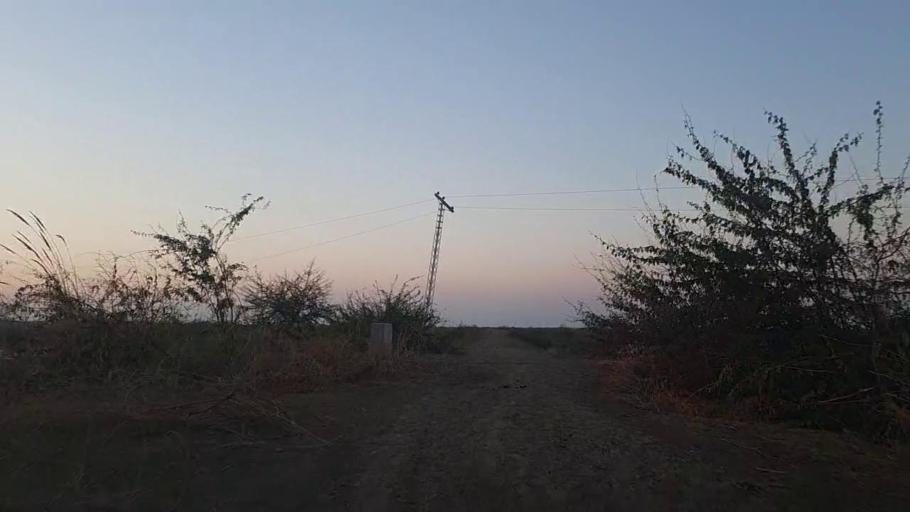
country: PK
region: Sindh
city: Tando Mittha Khan
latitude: 26.0684
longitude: 69.1589
